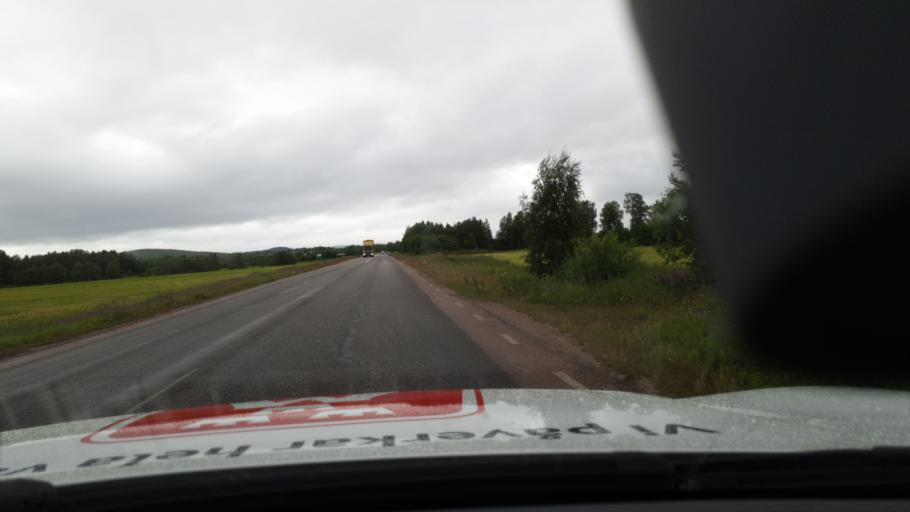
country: SE
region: Norrbotten
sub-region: Overtornea Kommun
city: OEvertornea
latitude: 66.4108
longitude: 23.6241
